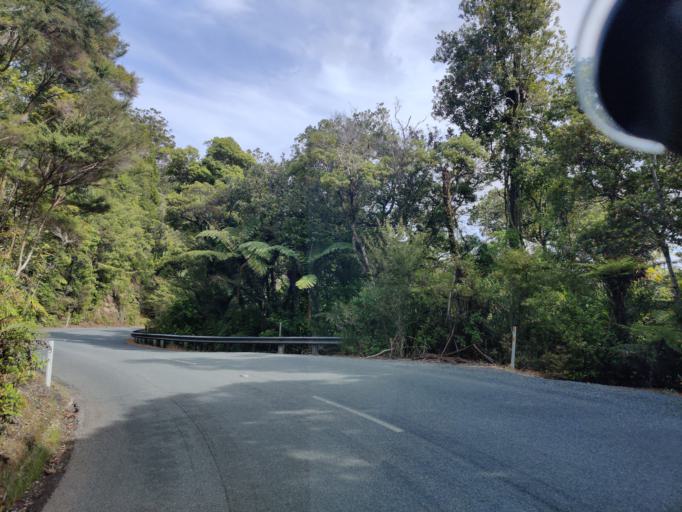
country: NZ
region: Northland
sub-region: Kaipara District
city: Dargaville
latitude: -35.6474
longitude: 173.5599
